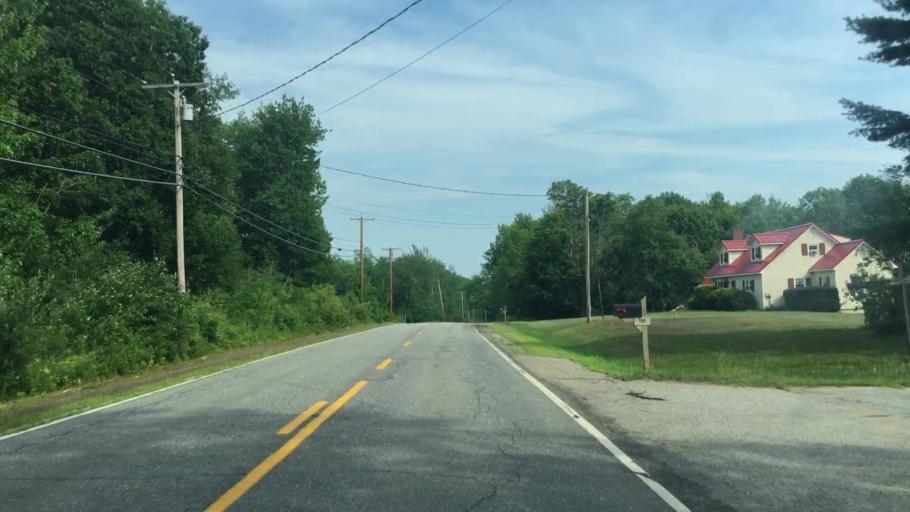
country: US
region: Maine
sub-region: Lincoln County
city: Waldoboro
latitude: 44.0723
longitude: -69.3660
